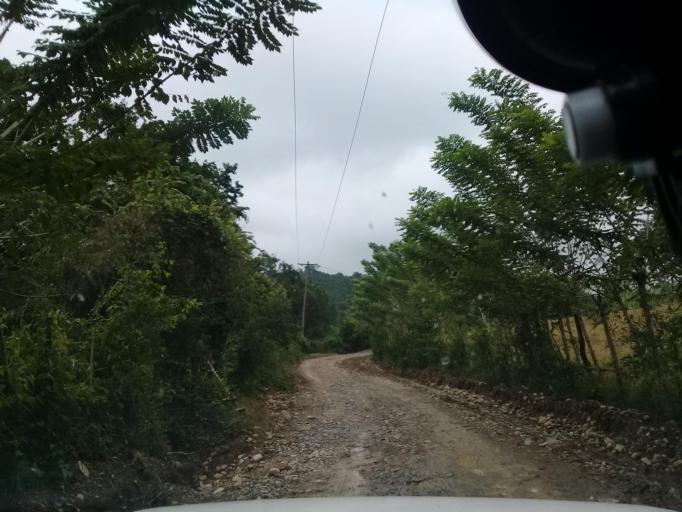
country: MX
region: Veracruz
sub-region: Chalma
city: San Pedro Coyutla
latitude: 21.2367
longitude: -98.4186
